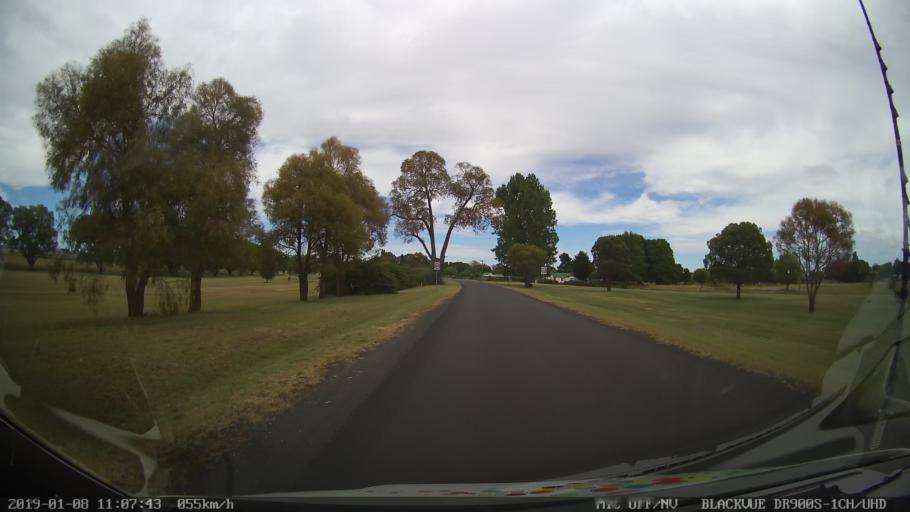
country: AU
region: New South Wales
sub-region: Guyra
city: Guyra
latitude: -30.2174
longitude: 151.6630
